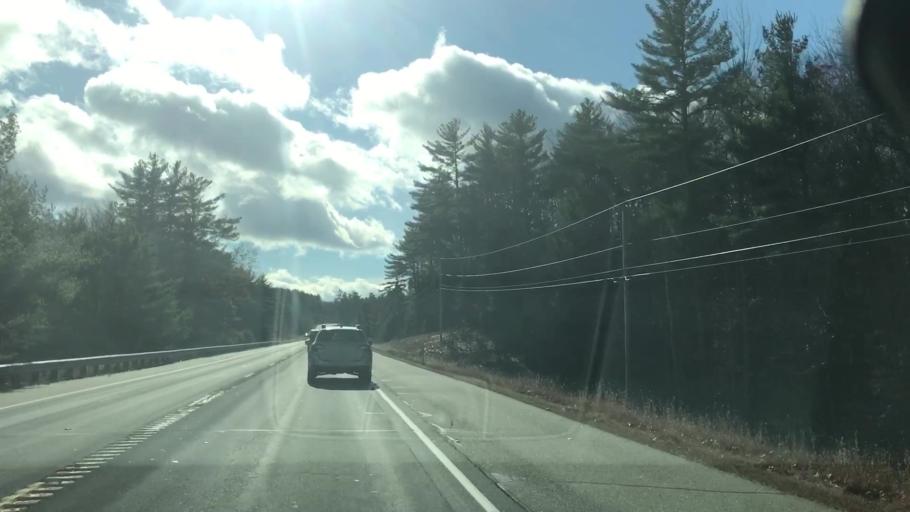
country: US
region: New Hampshire
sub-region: Carroll County
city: Wolfeboro
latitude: 43.5326
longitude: -71.2040
